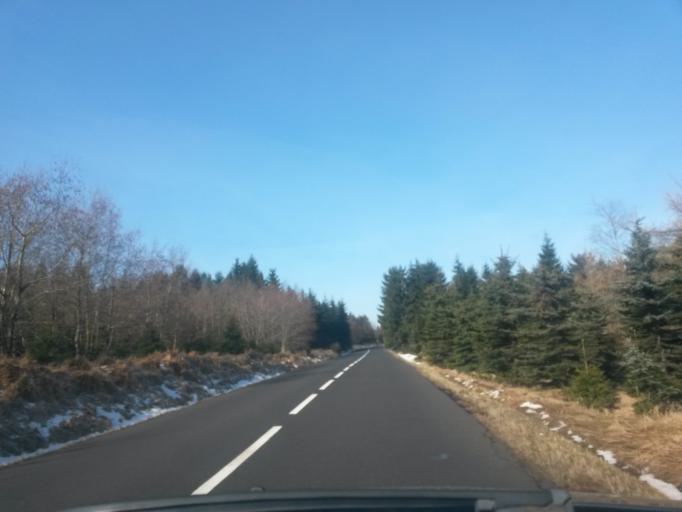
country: CZ
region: Ustecky
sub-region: Okres Chomutov
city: Kovarska
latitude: 50.4105
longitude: 13.0423
